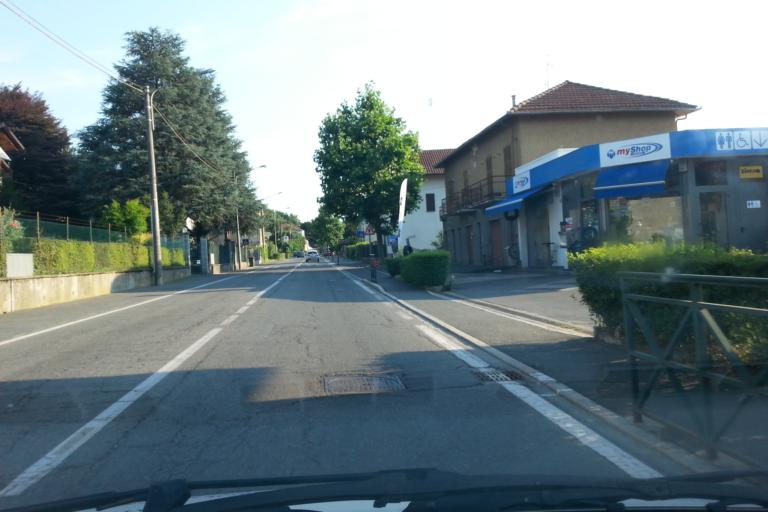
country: IT
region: Piedmont
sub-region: Provincia di Torino
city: Avigliana
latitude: 45.0755
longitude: 7.3951
